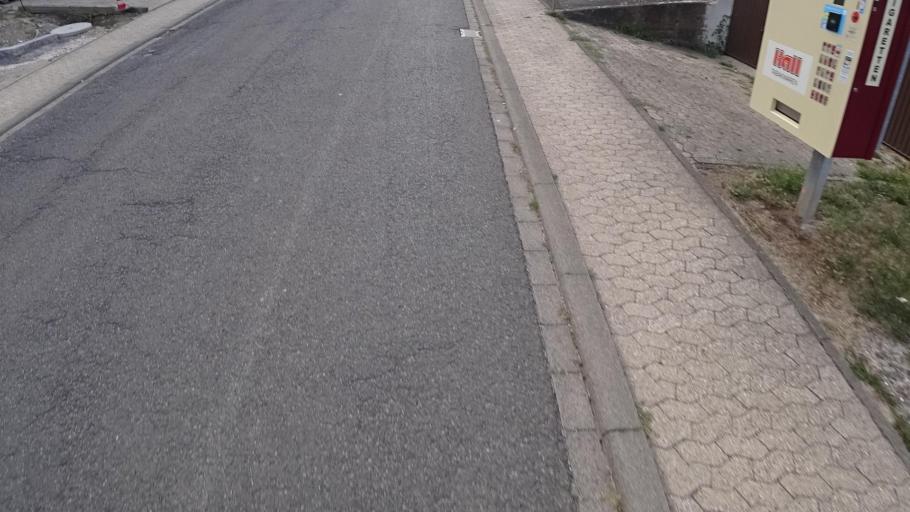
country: DE
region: Rheinland-Pfalz
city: Dichtelbach
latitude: 50.0093
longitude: 7.6955
